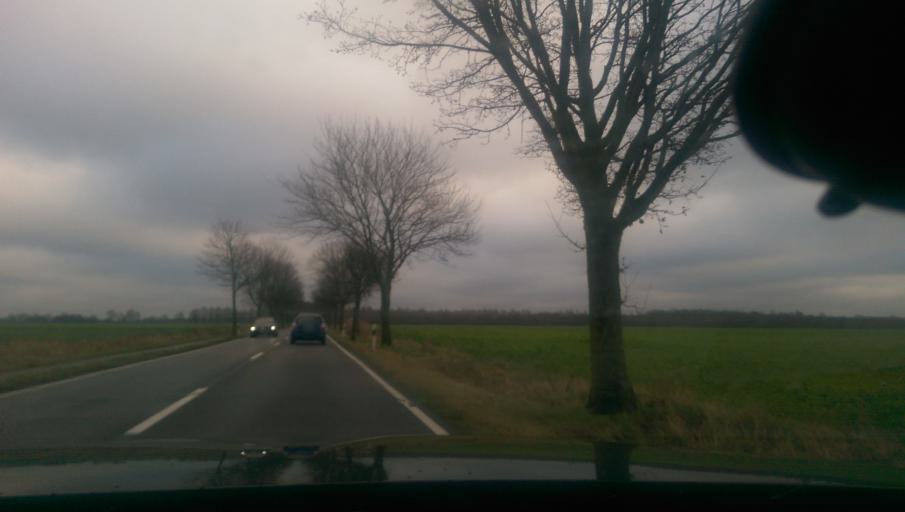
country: DE
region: Lower Saxony
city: Arpke
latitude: 52.3867
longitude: 10.0447
